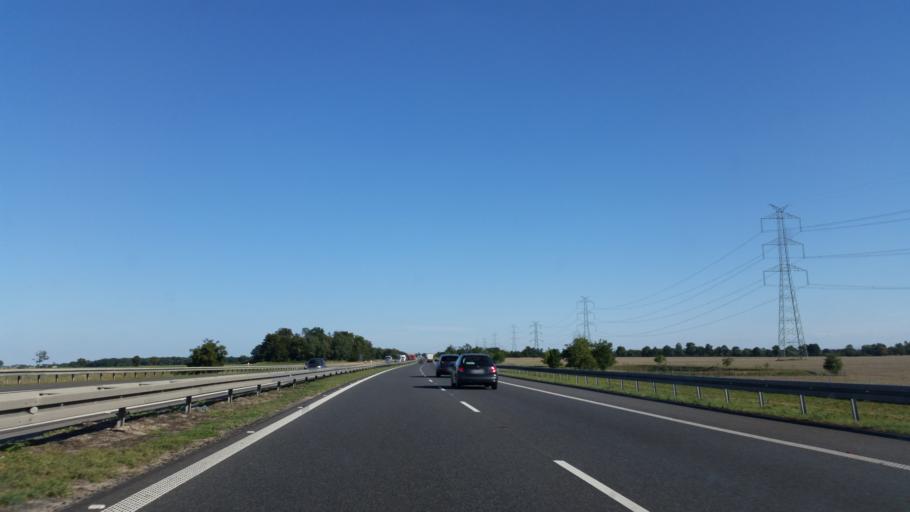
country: PL
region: Lower Silesian Voivodeship
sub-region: Powiat strzelinski
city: Wiazow
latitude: 50.8331
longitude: 17.2862
